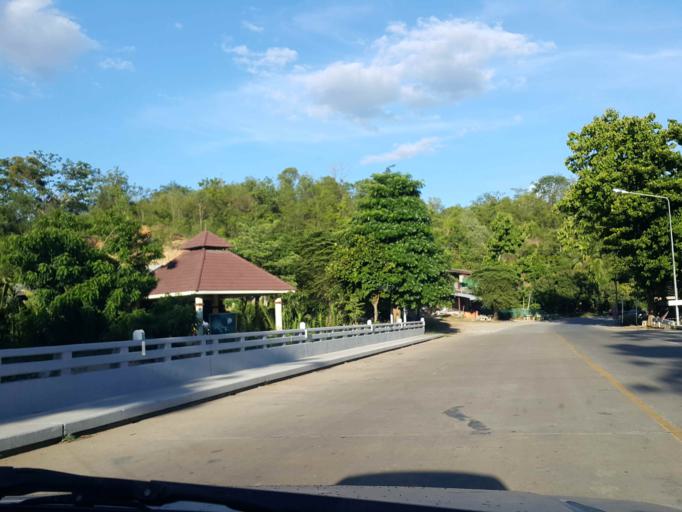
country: TH
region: Chiang Mai
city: Chom Thong
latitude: 18.4923
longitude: 98.6715
